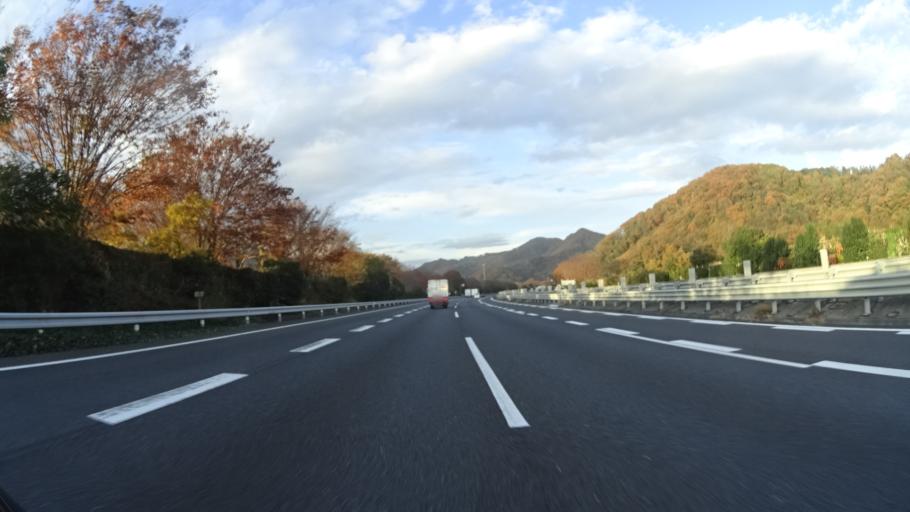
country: JP
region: Tochigi
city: Tanuma
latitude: 36.3627
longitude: 139.6272
